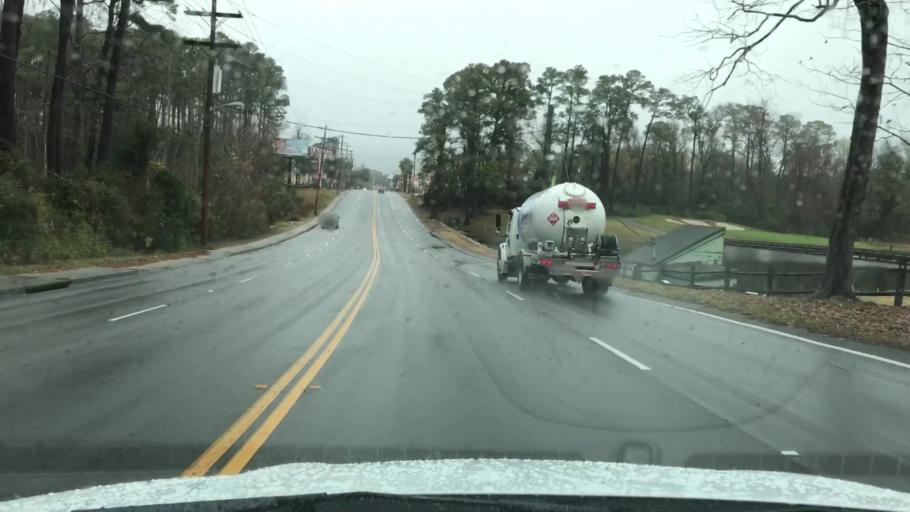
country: US
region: South Carolina
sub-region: Horry County
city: North Myrtle Beach
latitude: 33.7727
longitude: -78.7895
